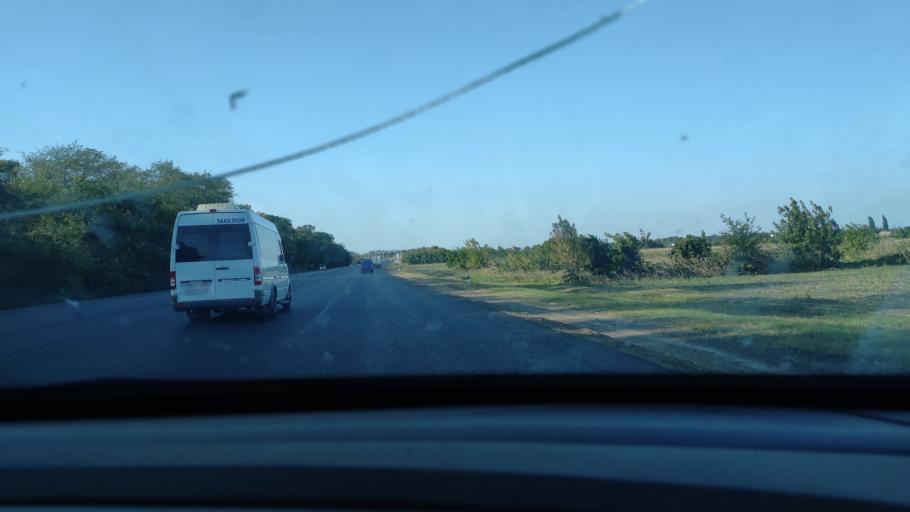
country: RU
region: Krasnodarskiy
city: Medvedovskaya
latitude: 45.5091
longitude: 38.9413
